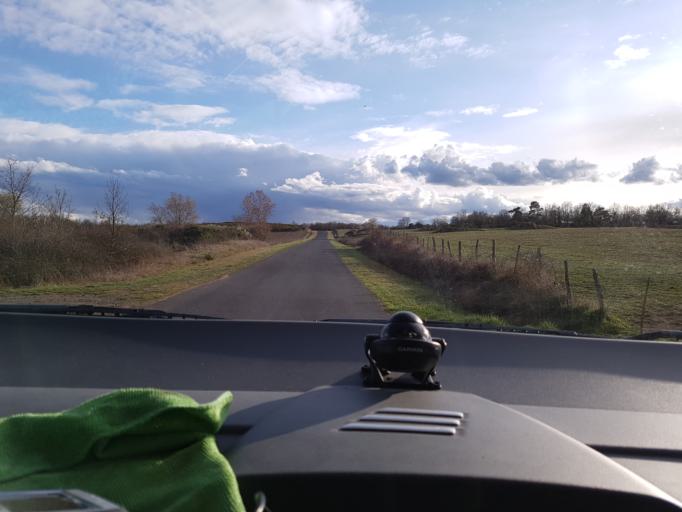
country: FR
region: Auvergne
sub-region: Departement de la Haute-Loire
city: Lempdes-sur-Allagnon
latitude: 45.3709
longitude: 3.2571
